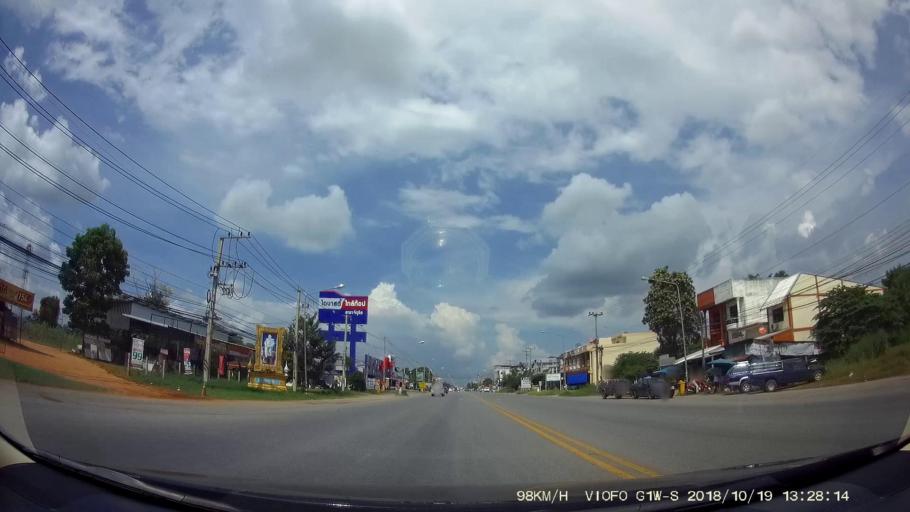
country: TH
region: Chaiyaphum
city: Chatturat
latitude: 15.5596
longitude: 101.8473
